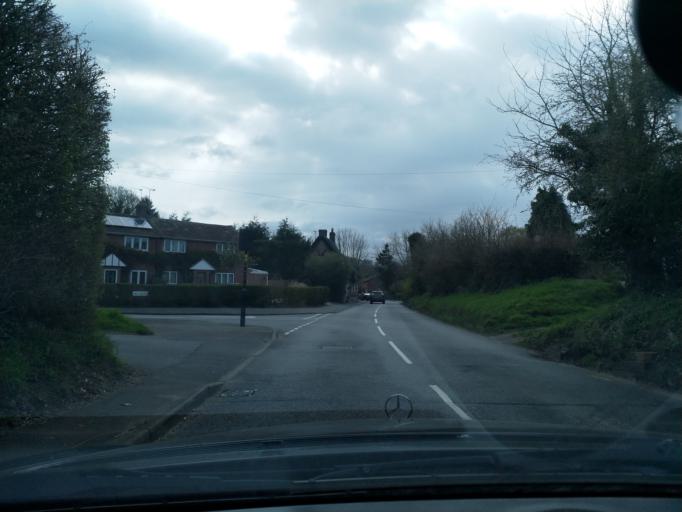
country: GB
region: England
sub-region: Coventry
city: Coventry
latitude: 52.3534
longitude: -1.5200
